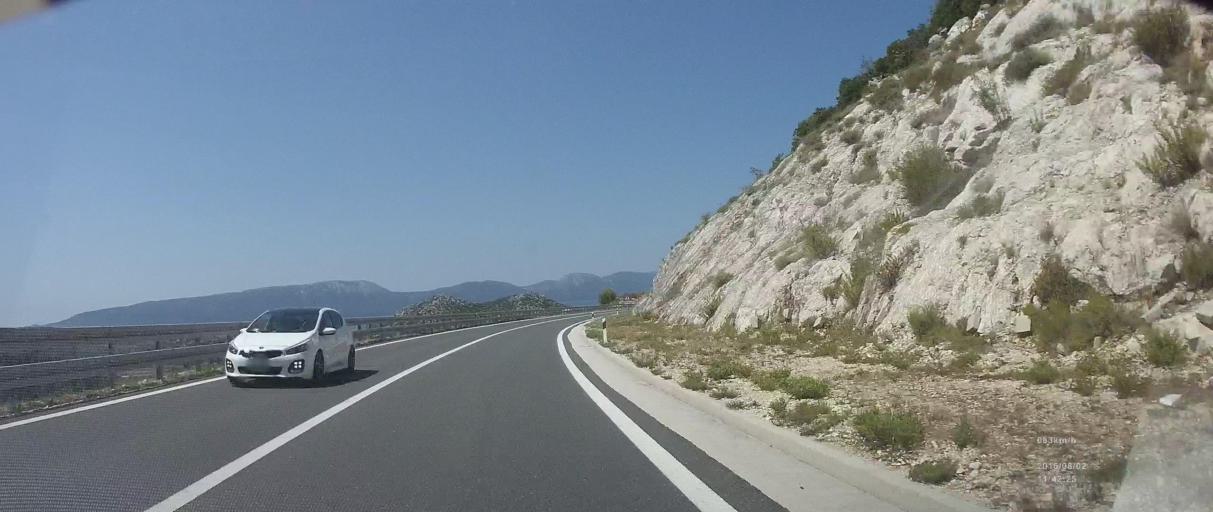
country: HR
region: Dubrovacko-Neretvanska
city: Komin
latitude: 43.0535
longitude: 17.4877
